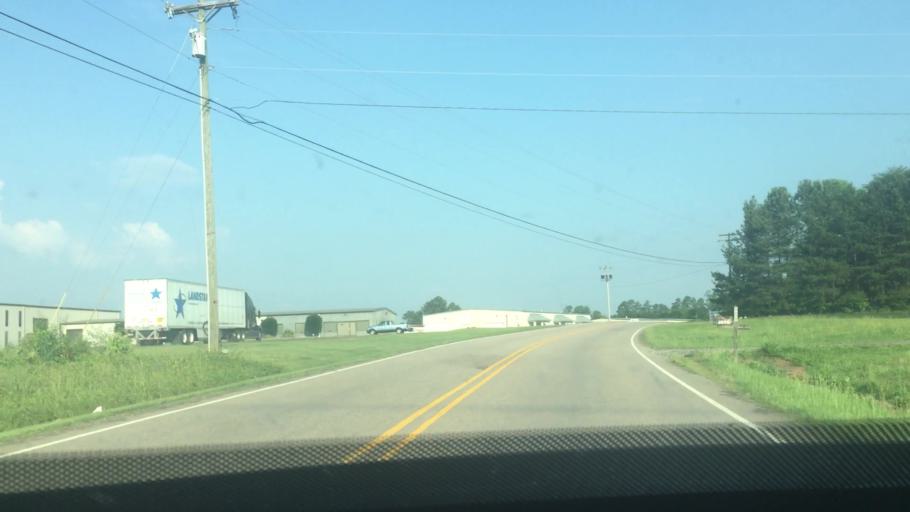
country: US
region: North Carolina
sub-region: Iredell County
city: Mooresville
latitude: 35.5817
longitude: -80.7351
